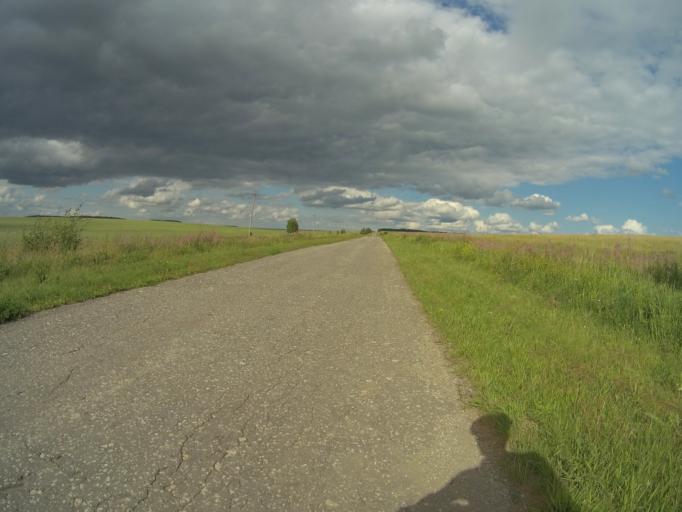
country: RU
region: Vladimir
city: Suzdal'
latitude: 56.3015
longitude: 40.3711
